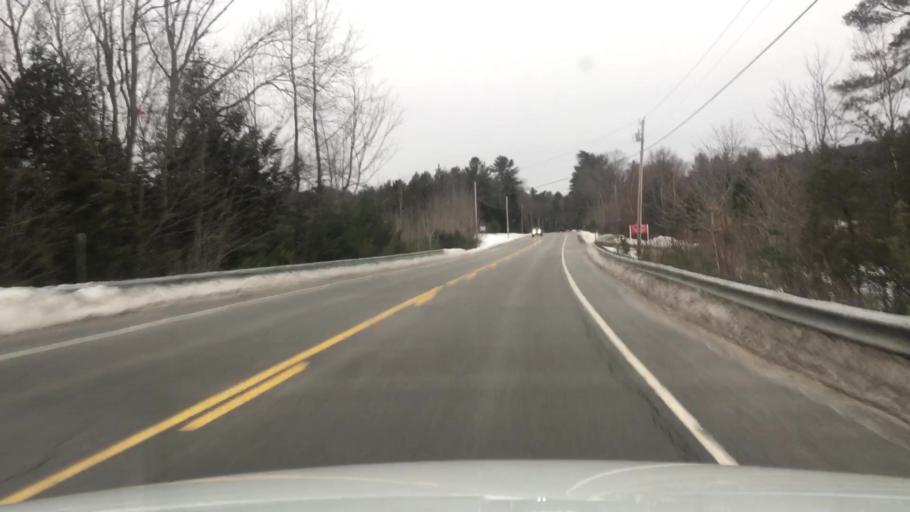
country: US
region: Maine
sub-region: York County
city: Limerick
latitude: 43.7192
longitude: -70.8142
